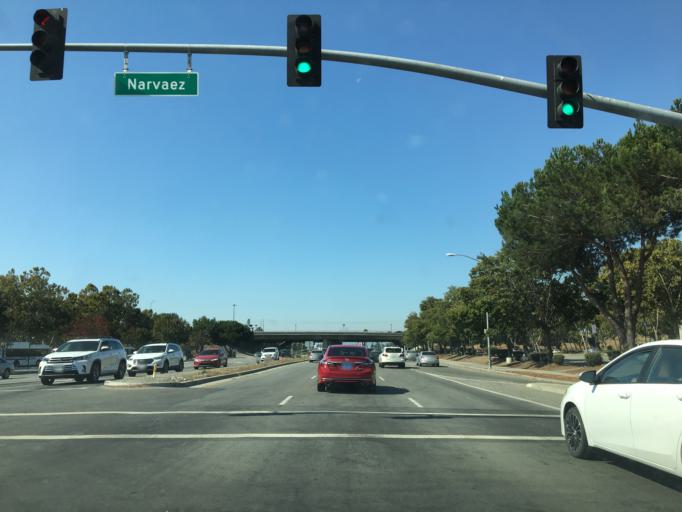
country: US
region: California
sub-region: Santa Clara County
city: Seven Trees
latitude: 37.2745
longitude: -121.8604
